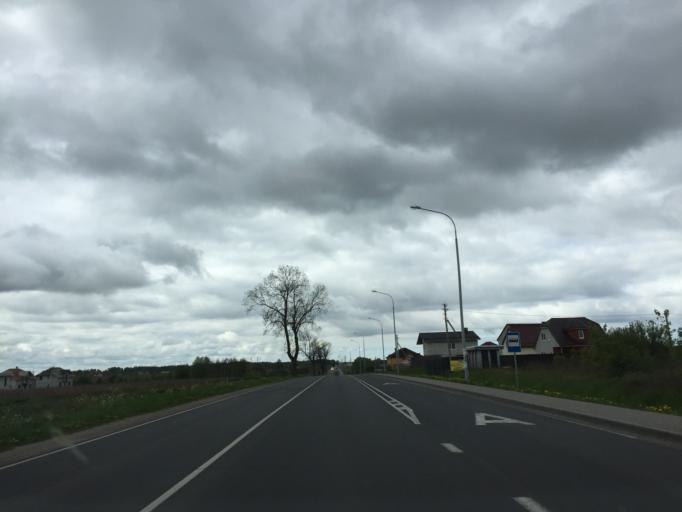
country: RU
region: Kaliningrad
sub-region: Gorod Kaliningrad
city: Kaliningrad
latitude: 54.6654
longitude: 20.4174
